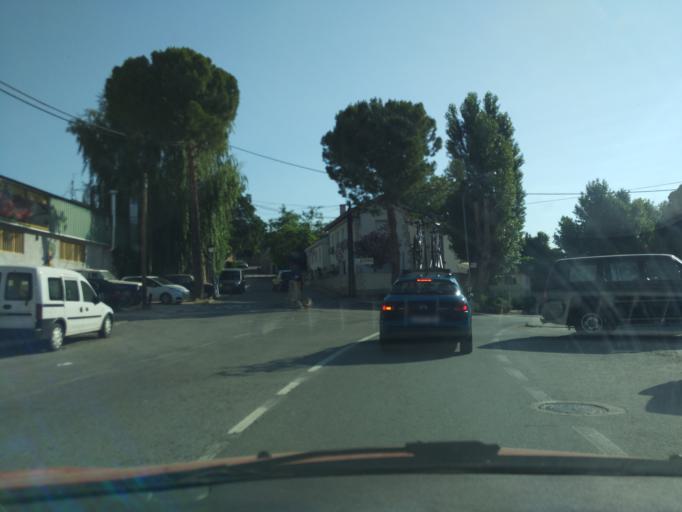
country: ES
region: Madrid
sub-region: Provincia de Madrid
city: Ambite
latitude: 40.3267
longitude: -3.1835
